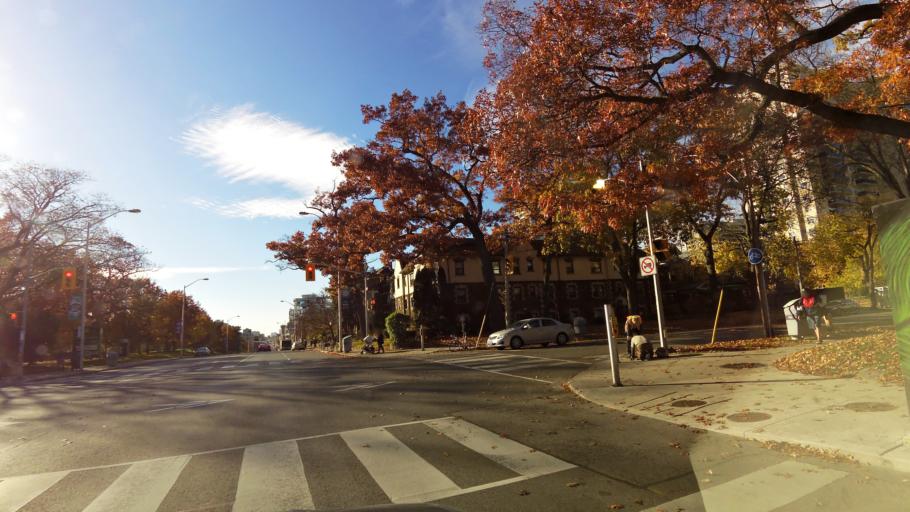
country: CA
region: Ontario
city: Toronto
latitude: 43.6536
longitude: -79.4651
